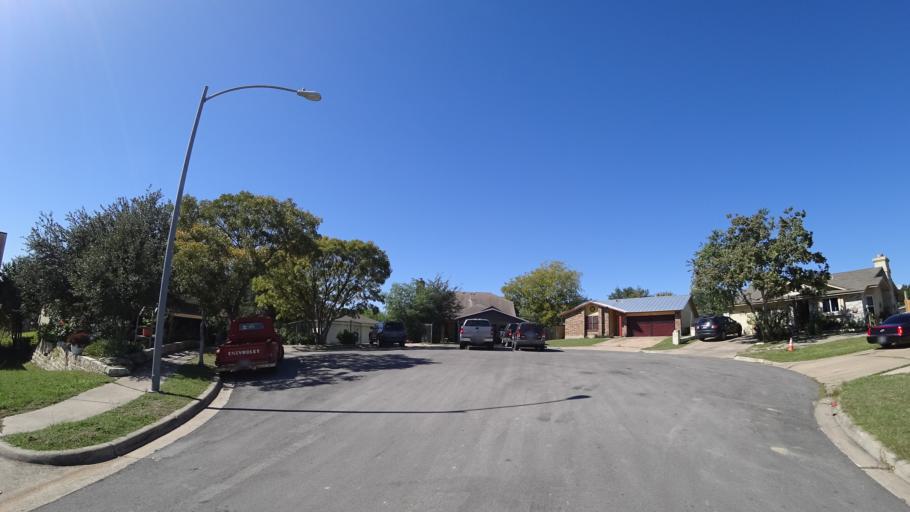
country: US
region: Texas
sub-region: Travis County
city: Hornsby Bend
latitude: 30.3021
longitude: -97.6388
